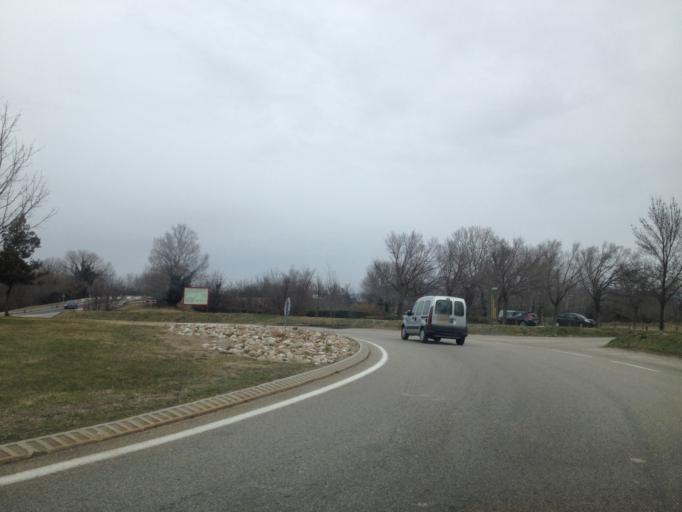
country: FR
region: Provence-Alpes-Cote d'Azur
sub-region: Departement du Vaucluse
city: Jonquieres
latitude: 44.1060
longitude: 4.9162
